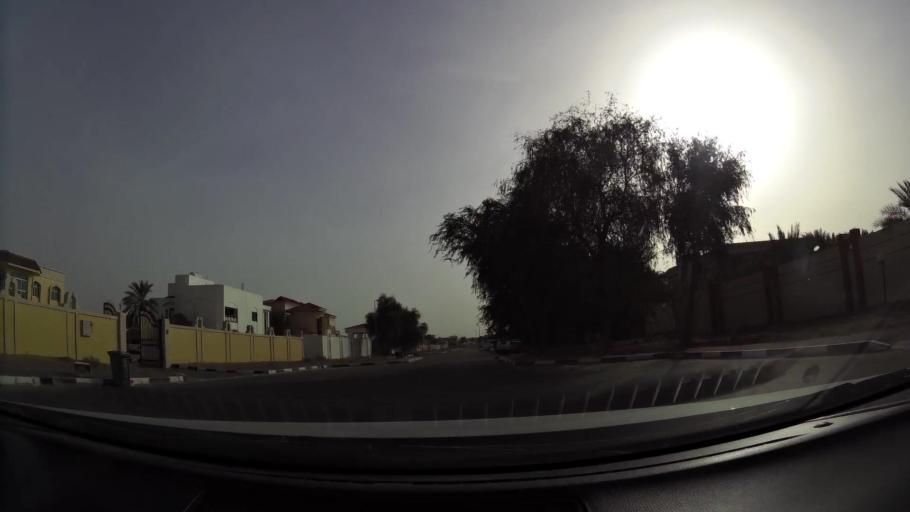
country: AE
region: Abu Dhabi
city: Al Ain
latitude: 24.2258
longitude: 55.6666
